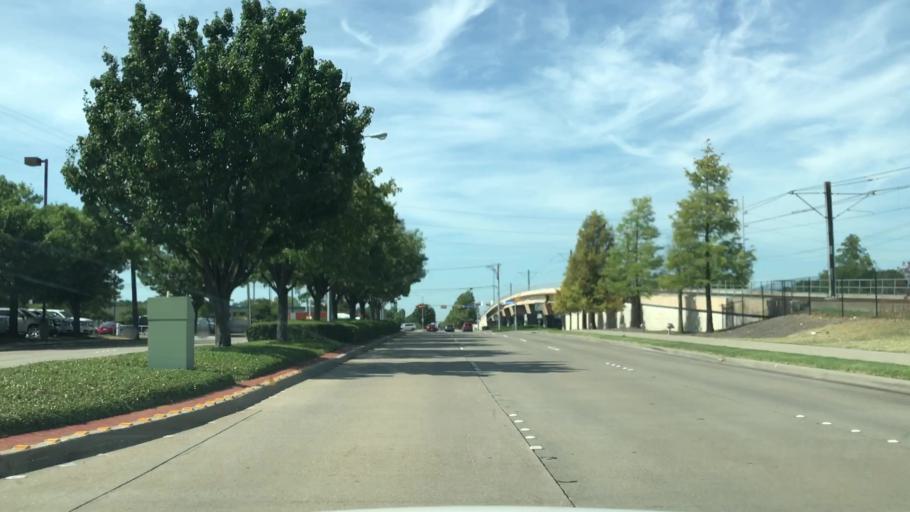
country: US
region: Texas
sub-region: Dallas County
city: Richardson
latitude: 32.9622
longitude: -96.7234
